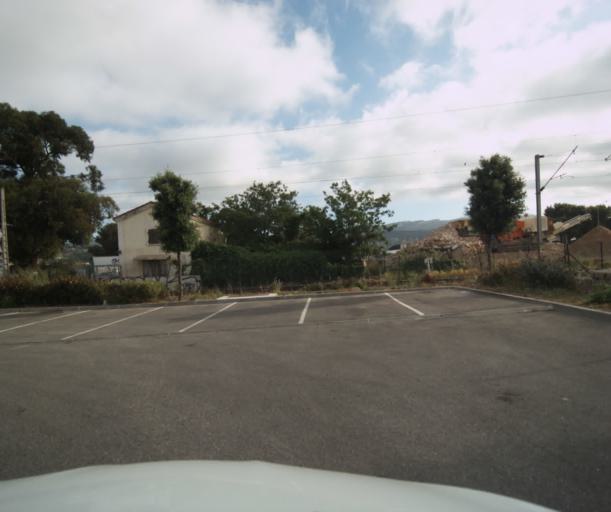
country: FR
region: Provence-Alpes-Cote d'Azur
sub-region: Departement du Var
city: Ollioules
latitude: 43.1195
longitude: 5.8422
